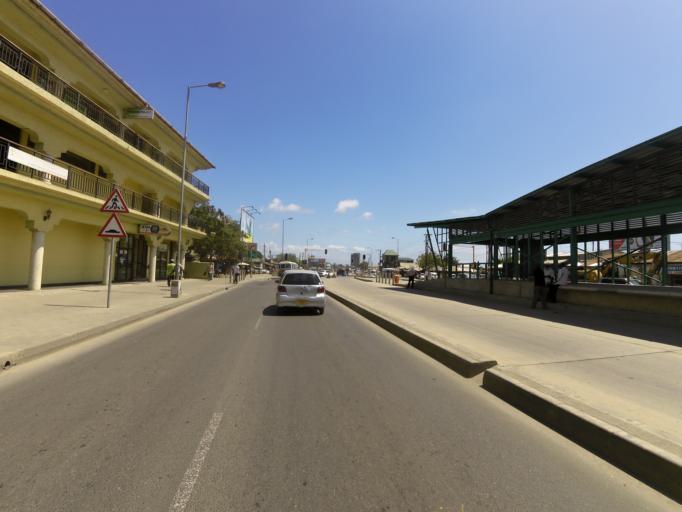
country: TZ
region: Dar es Salaam
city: Magomeni
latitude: -6.7909
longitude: 39.2637
